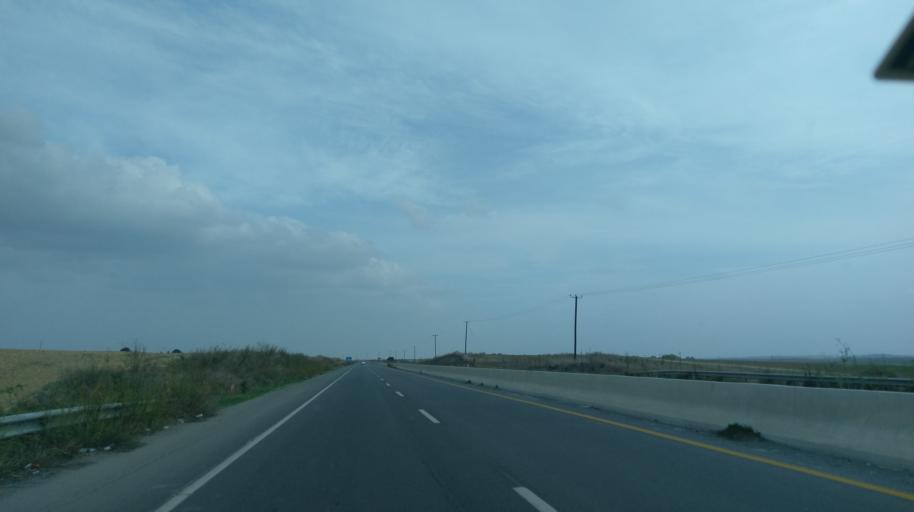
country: CY
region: Lefkosia
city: Mammari
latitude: 35.2116
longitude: 33.2105
